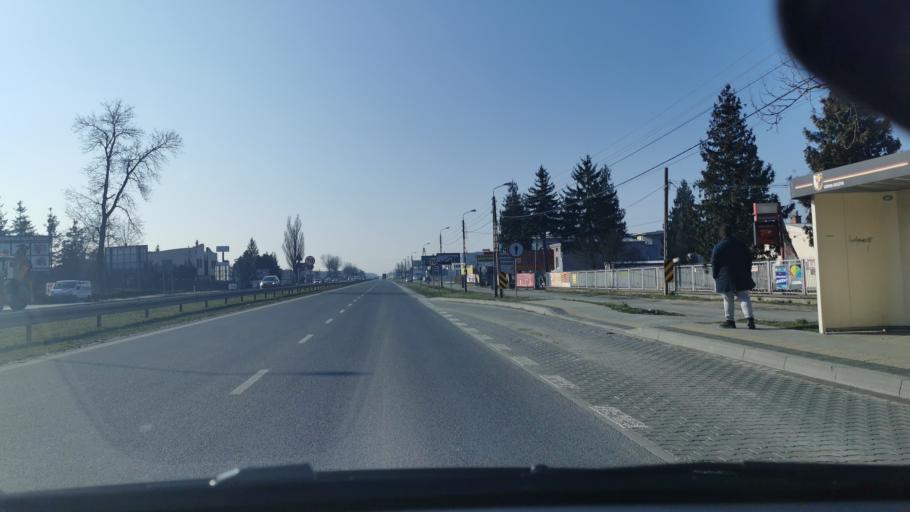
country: PL
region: Masovian Voivodeship
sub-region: Powiat pruszkowski
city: Nowe Grocholice
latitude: 52.1240
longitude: 20.8946
